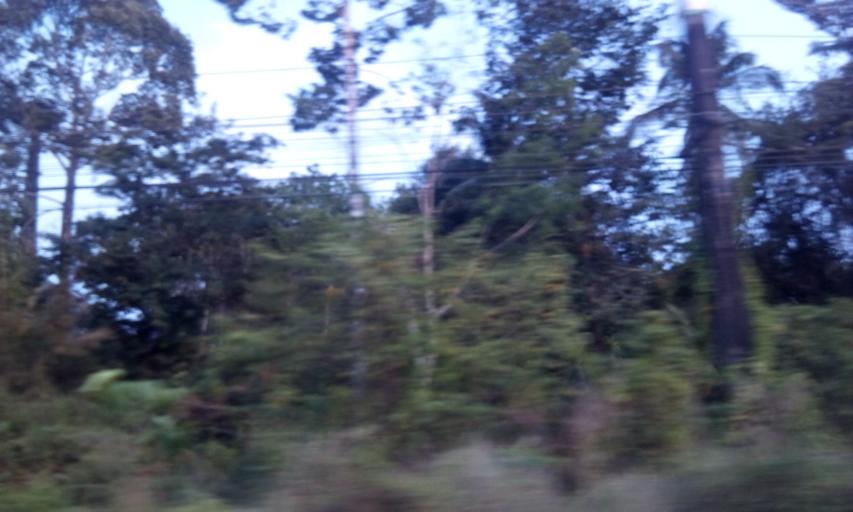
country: TH
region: Trat
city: Khao Saming
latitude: 12.3406
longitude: 102.3735
